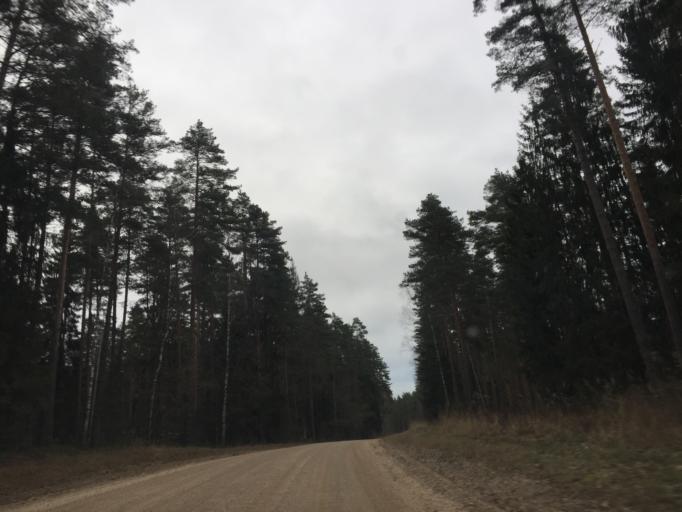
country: LV
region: Cesu Rajons
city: Cesis
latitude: 57.3325
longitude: 25.2573
